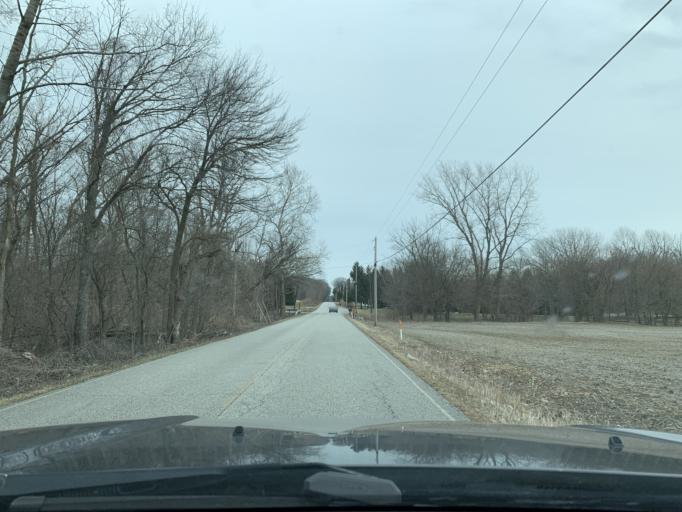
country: US
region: Indiana
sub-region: Porter County
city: Chesterton
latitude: 41.5859
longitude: -87.0103
